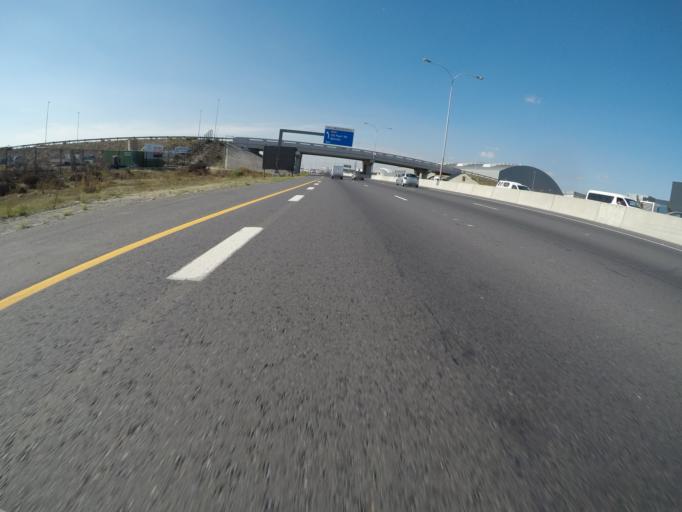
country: ZA
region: Western Cape
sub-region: City of Cape Town
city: Kraaifontein
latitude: -33.9005
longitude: 18.6764
